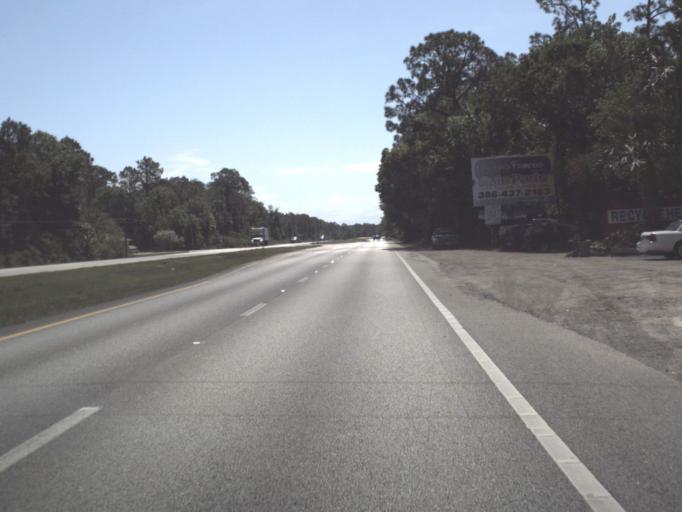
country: US
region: Florida
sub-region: Flagler County
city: Bunnell
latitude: 29.4257
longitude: -81.2209
